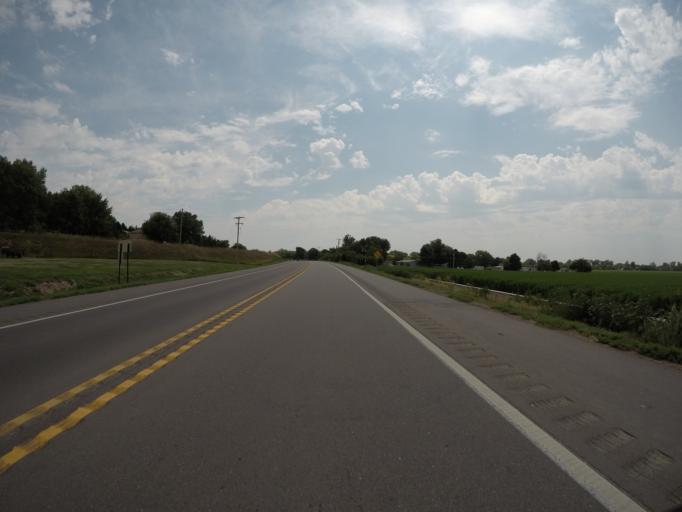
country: US
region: Nebraska
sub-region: Buffalo County
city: Kearney
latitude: 40.6985
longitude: -99.1462
